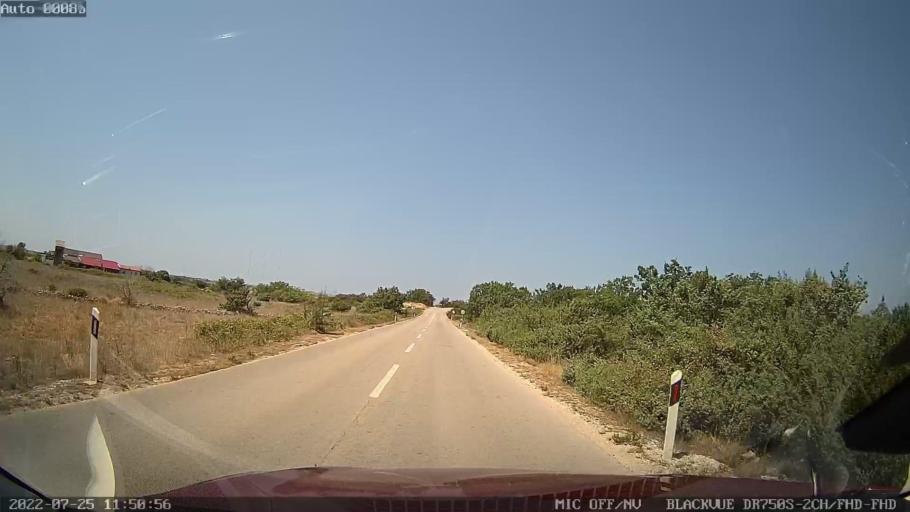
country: HR
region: Zadarska
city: Vrsi
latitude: 44.2376
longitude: 15.2578
